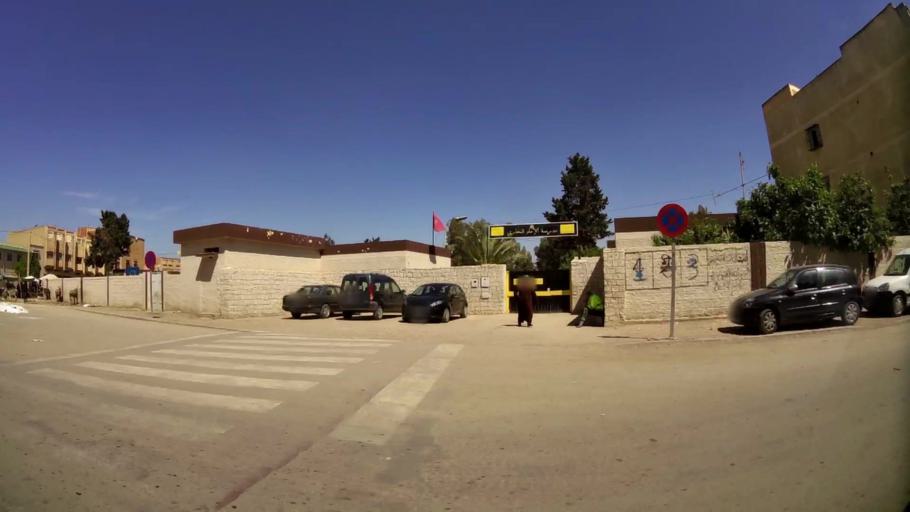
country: MA
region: Oriental
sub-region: Oujda-Angad
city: Oujda
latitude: 34.6857
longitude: -1.9321
